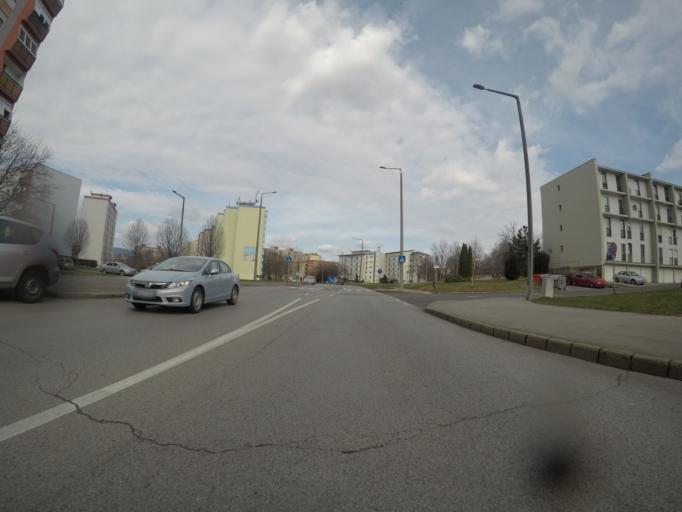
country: HU
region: Baranya
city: Pecs
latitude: 46.0388
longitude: 18.2278
